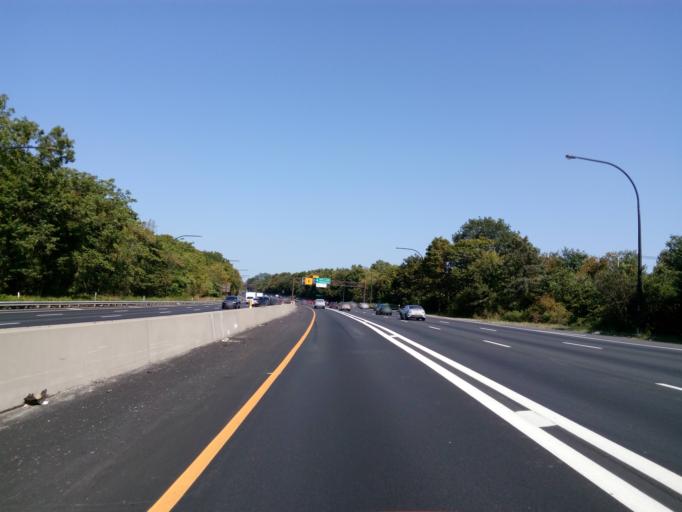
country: US
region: New York
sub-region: Nassau County
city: Old Westbury
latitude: 40.7798
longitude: -73.6043
